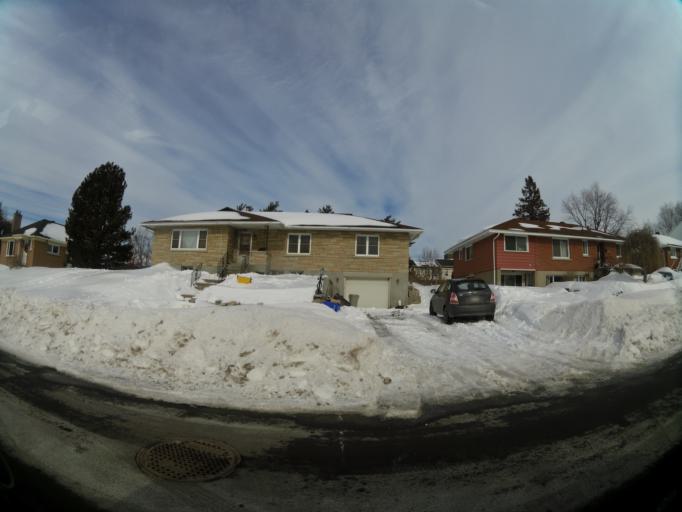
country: CA
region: Ontario
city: Ottawa
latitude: 45.4452
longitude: -75.6120
